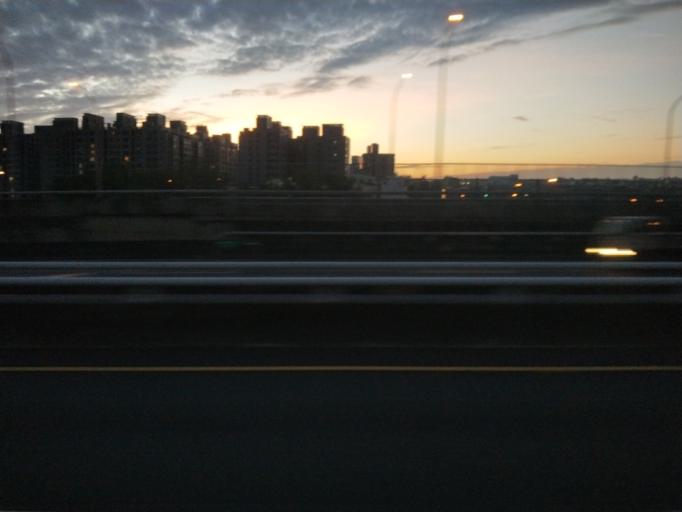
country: TW
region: Taiwan
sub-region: Taichung City
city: Taichung
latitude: 24.1529
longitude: 120.6200
